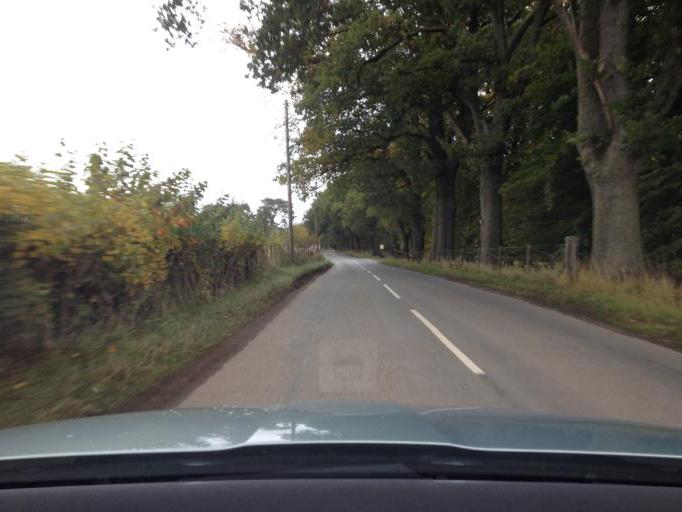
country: GB
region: Scotland
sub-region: Perth and Kinross
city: Stanley
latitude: 56.5145
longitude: -3.4077
